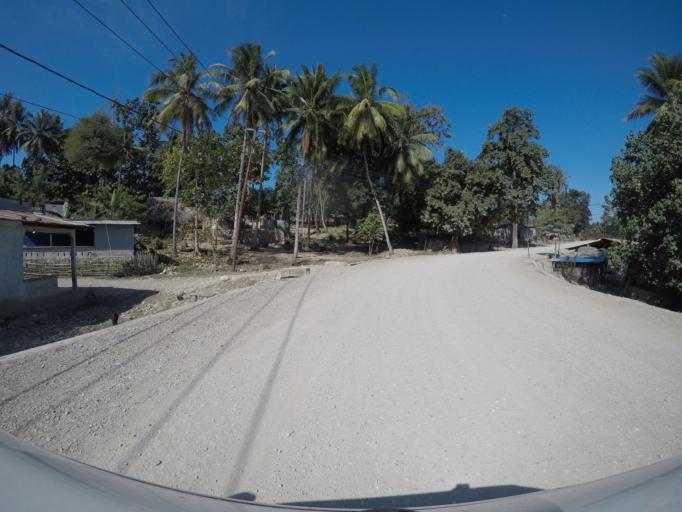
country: TL
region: Viqueque
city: Viqueque
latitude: -8.8413
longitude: 126.5131
